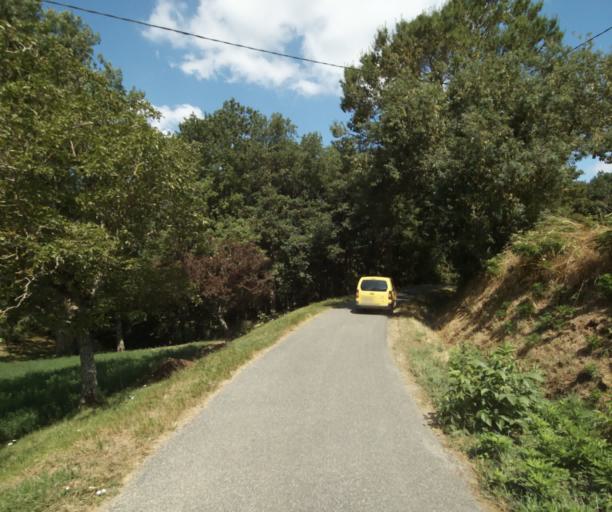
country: FR
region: Midi-Pyrenees
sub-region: Departement de la Haute-Garonne
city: Auriac-sur-Vendinelle
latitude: 43.4607
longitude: 1.8012
